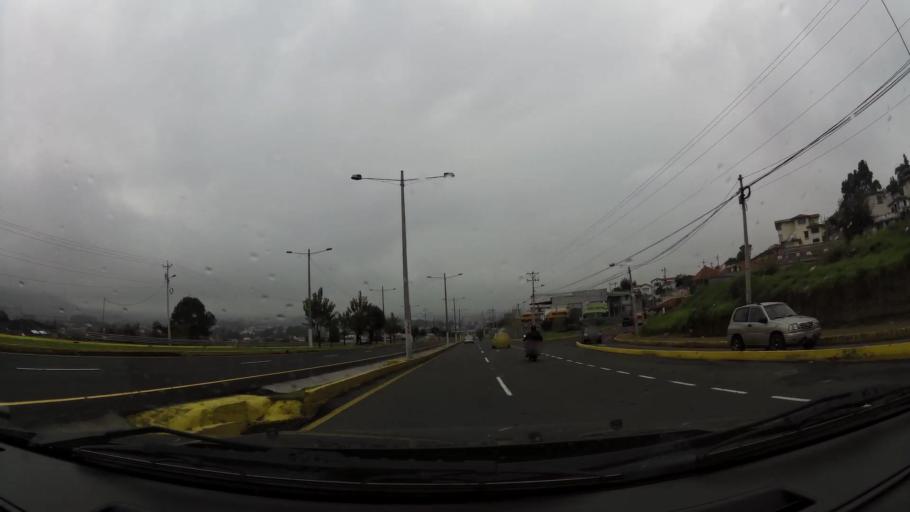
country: EC
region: Pichincha
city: Sangolqui
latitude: -0.2854
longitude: -78.4689
